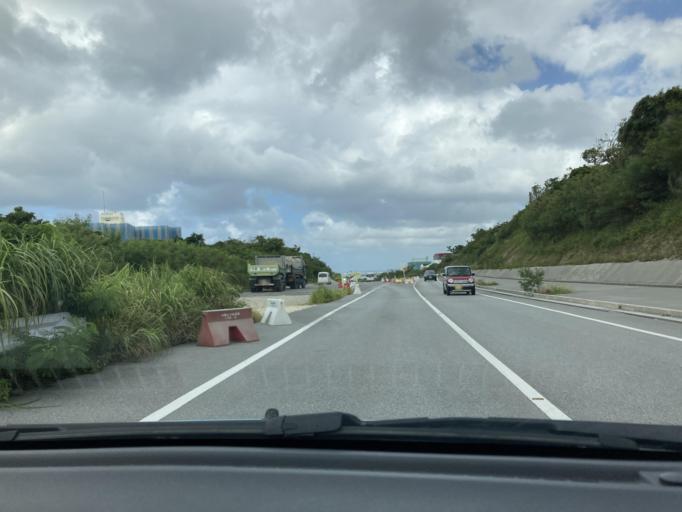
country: JP
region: Okinawa
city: Ginowan
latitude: 26.2658
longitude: 127.7091
